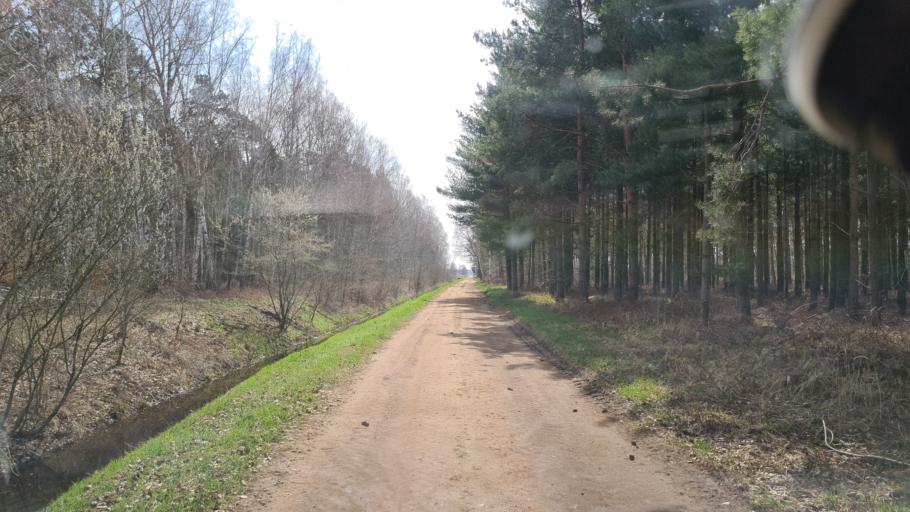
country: DE
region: Brandenburg
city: Bronkow
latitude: 51.6141
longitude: 13.9251
